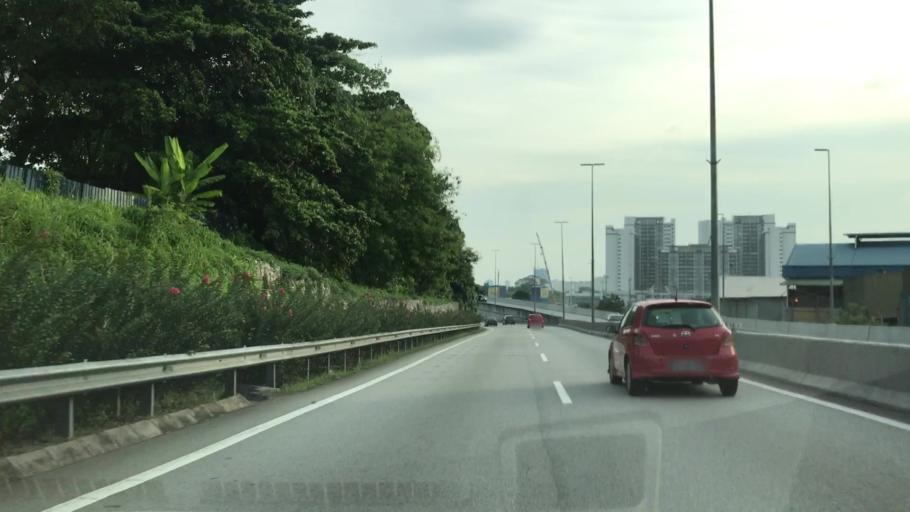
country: MY
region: Kuala Lumpur
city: Kuala Lumpur
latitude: 3.1100
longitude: 101.7095
